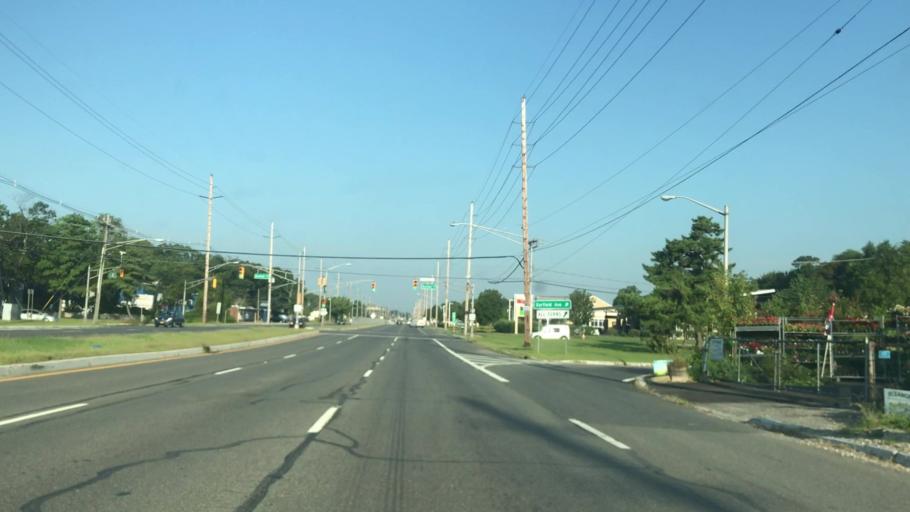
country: US
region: New Jersey
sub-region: Ocean County
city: Island Heights
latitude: 39.9503
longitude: -74.1301
